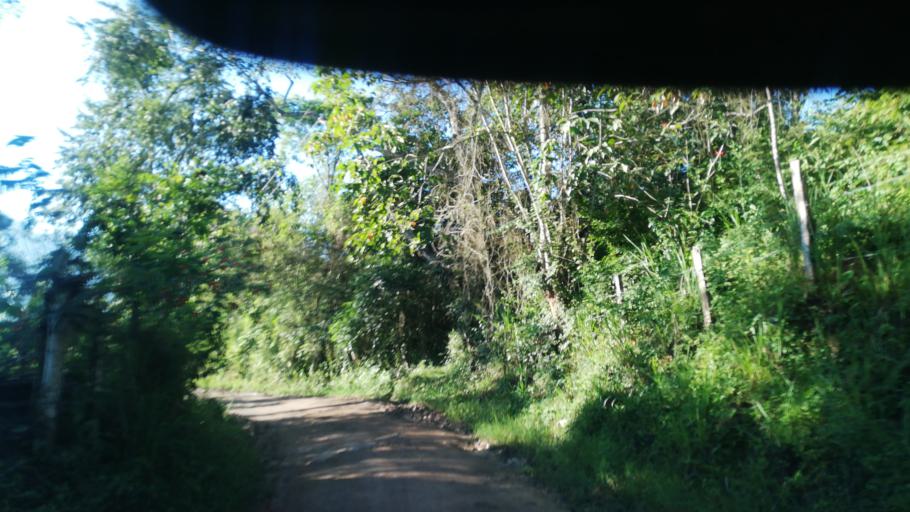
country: CO
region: Cundinamarca
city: Viani
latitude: 4.8405
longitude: -74.6243
